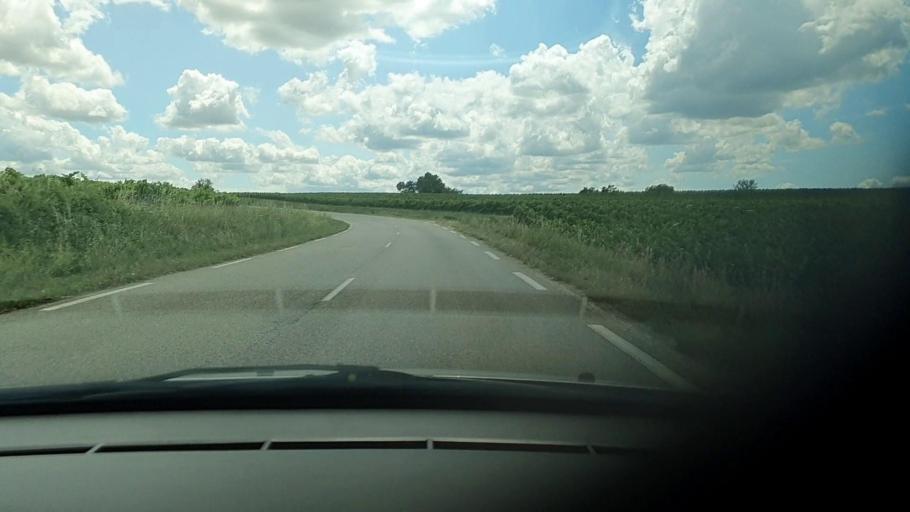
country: FR
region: Languedoc-Roussillon
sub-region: Departement du Gard
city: Moussac
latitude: 44.0177
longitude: 4.2315
